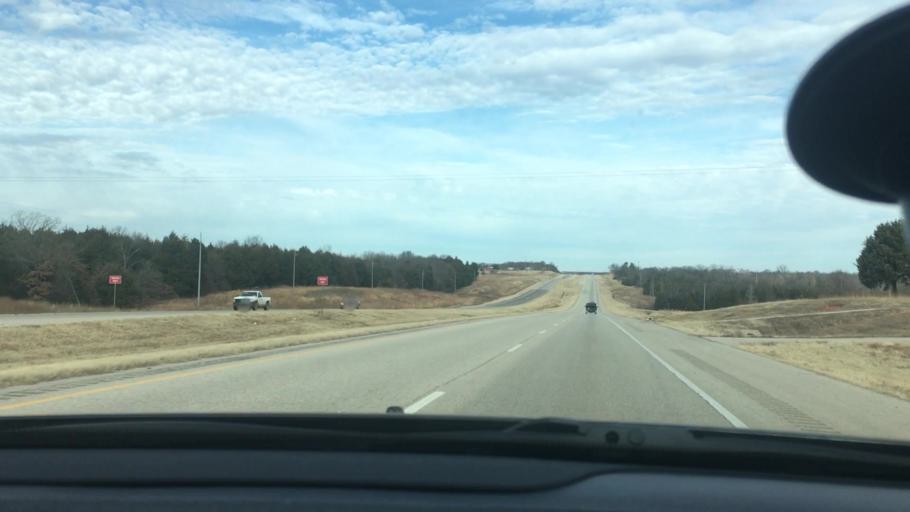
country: US
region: Oklahoma
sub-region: Pontotoc County
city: Byng
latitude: 34.9054
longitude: -96.6765
